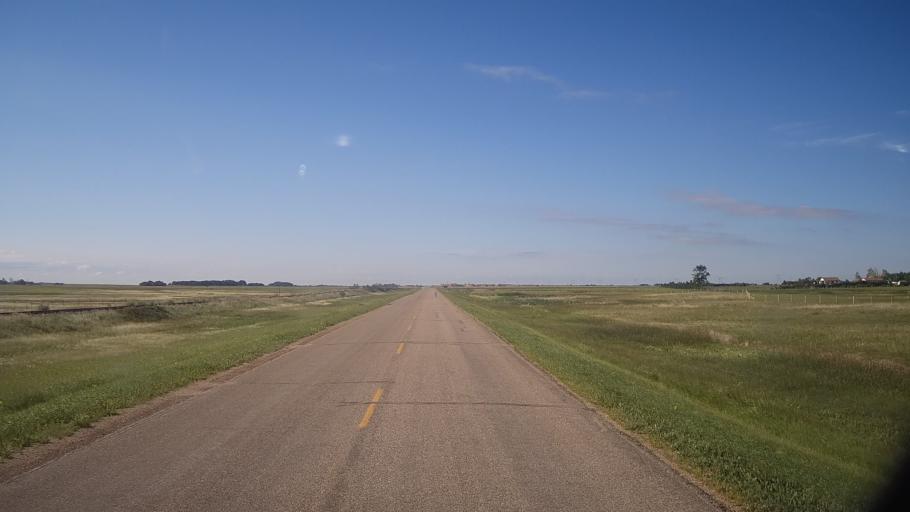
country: CA
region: Saskatchewan
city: Watrous
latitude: 51.7415
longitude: -105.2867
